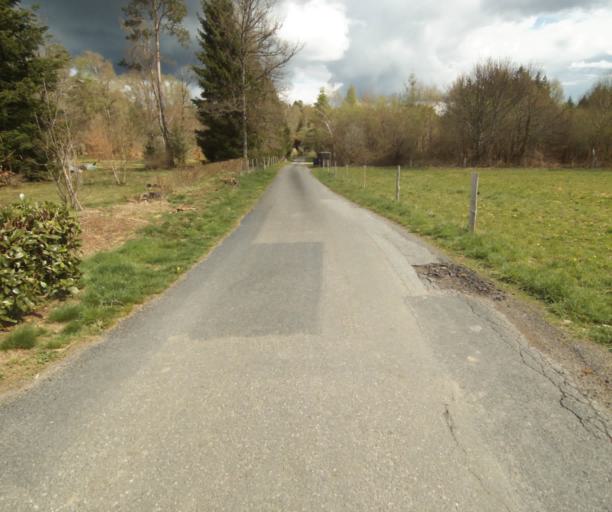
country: FR
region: Limousin
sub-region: Departement de la Correze
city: Laguenne
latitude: 45.2428
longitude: 1.8974
